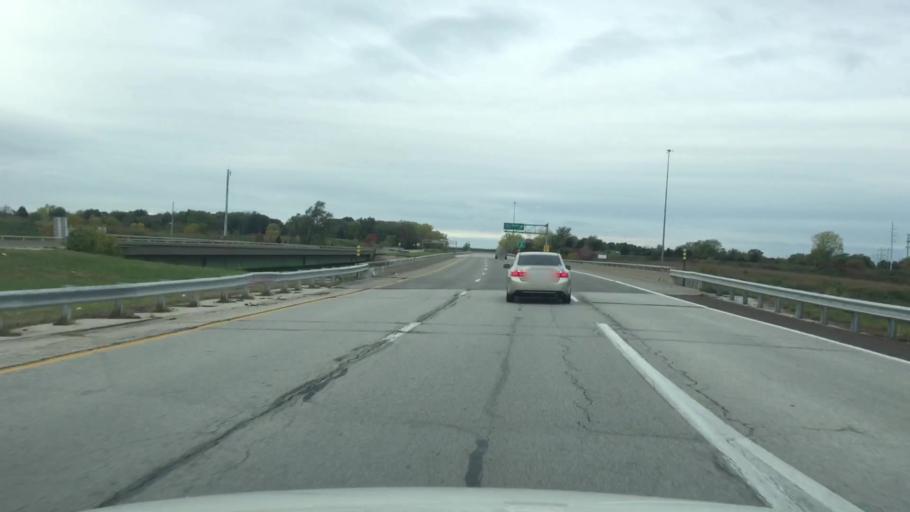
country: US
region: Kansas
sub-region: Wyandotte County
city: Edwardsville
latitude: 39.0108
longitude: -94.7840
